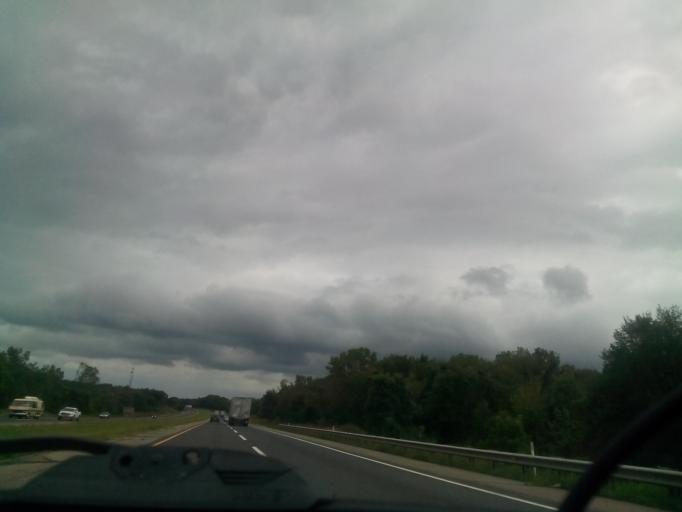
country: US
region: Indiana
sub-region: Steuben County
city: Fremont
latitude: 41.6559
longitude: -84.8443
